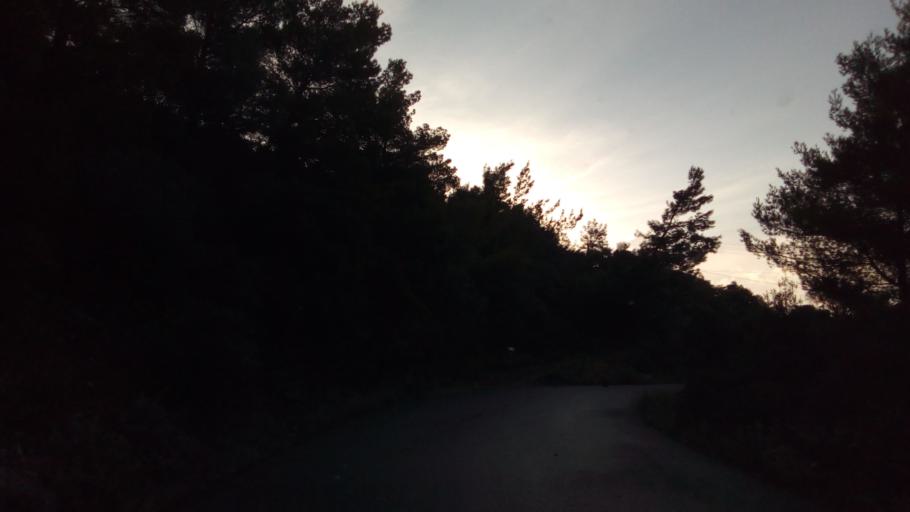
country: GR
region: West Greece
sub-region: Nomos Aitolias kai Akarnanias
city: Nafpaktos
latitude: 38.4002
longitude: 21.8323
